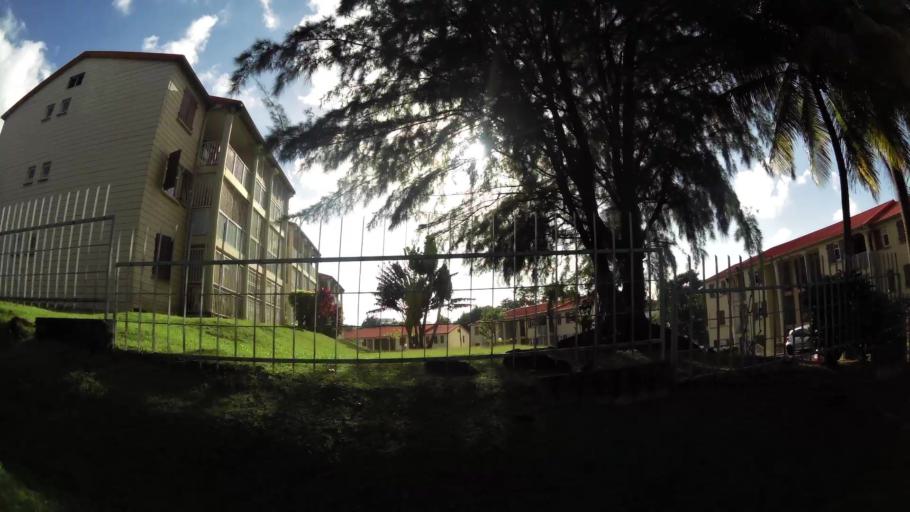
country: MQ
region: Martinique
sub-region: Martinique
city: Le Lamentin
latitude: 14.6221
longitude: -61.0161
